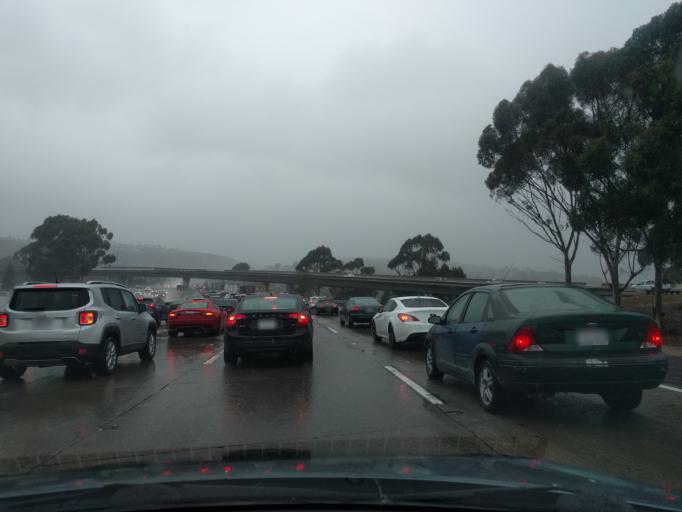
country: US
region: California
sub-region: San Diego County
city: San Diego
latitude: 32.7763
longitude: -117.1116
